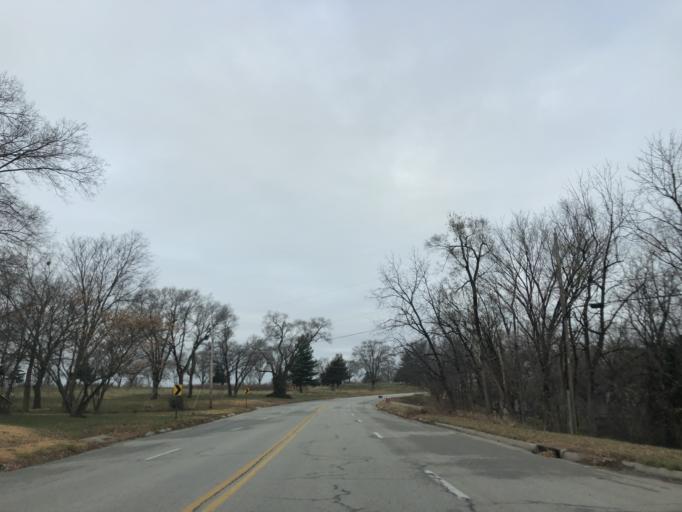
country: US
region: Kansas
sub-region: Johnson County
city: Gardner
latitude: 38.8440
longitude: -94.9289
